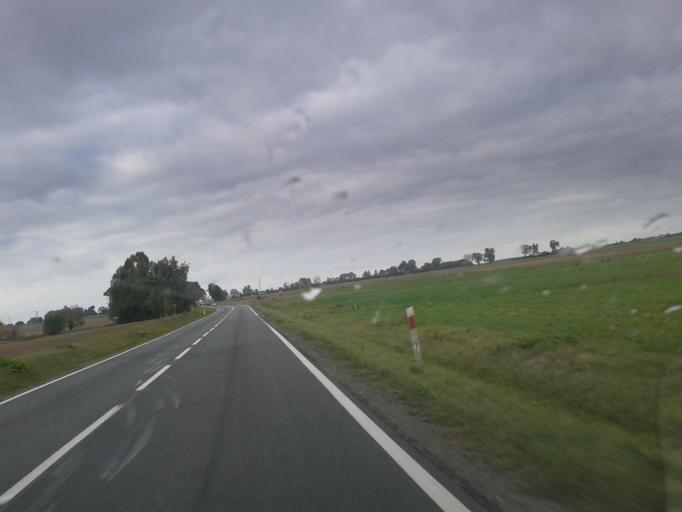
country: PL
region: Kujawsko-Pomorskie
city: Kamien Krajenski
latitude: 53.4928
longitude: 17.5118
